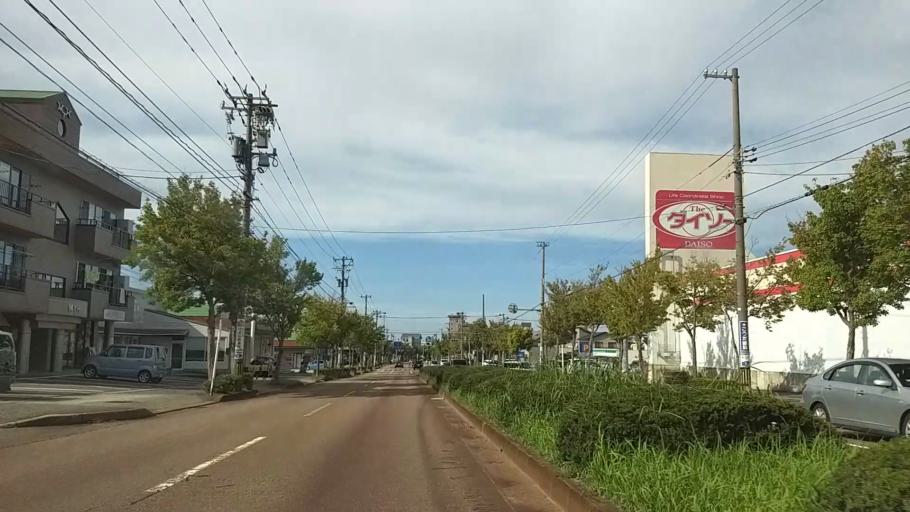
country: JP
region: Ishikawa
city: Nonoichi
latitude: 36.5262
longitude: 136.6388
